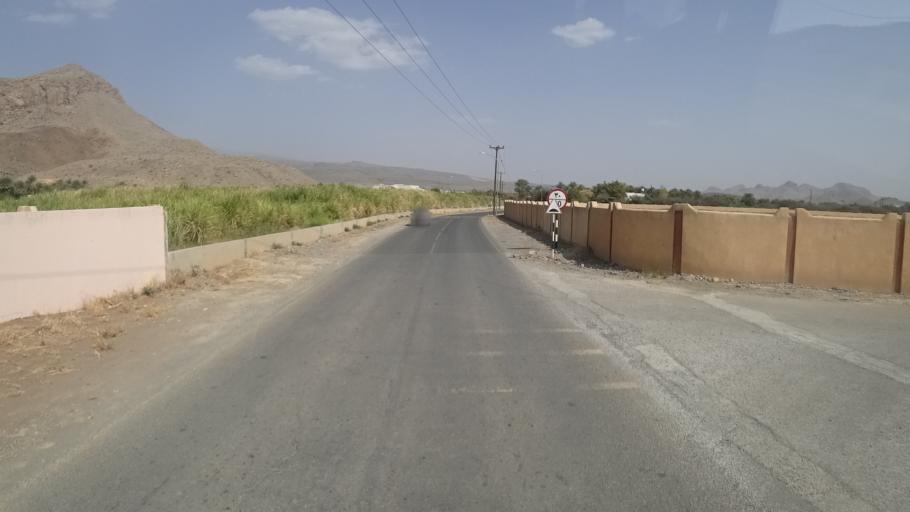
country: OM
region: Muhafazat ad Dakhiliyah
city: Bahla'
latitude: 23.1068
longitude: 57.2977
